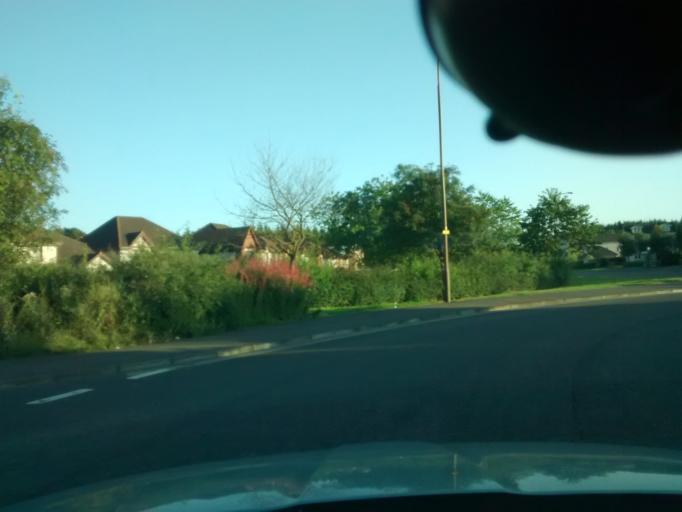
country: GB
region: Scotland
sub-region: West Lothian
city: Bathgate
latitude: 55.8921
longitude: -3.6209
